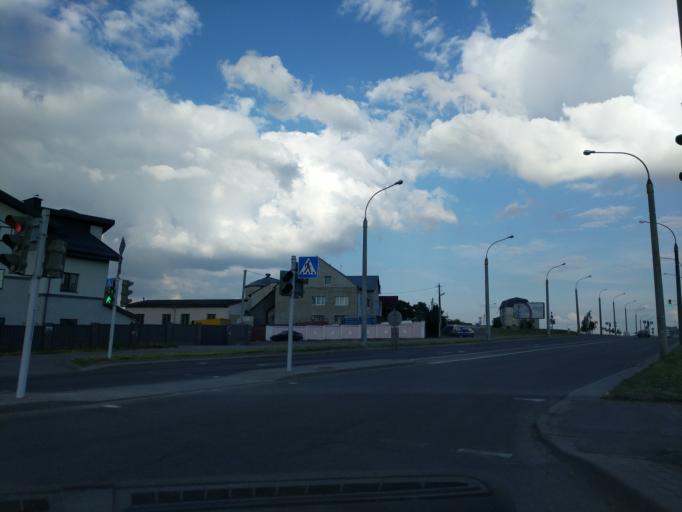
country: BY
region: Minsk
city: Zhdanovichy
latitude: 53.9355
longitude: 27.4320
